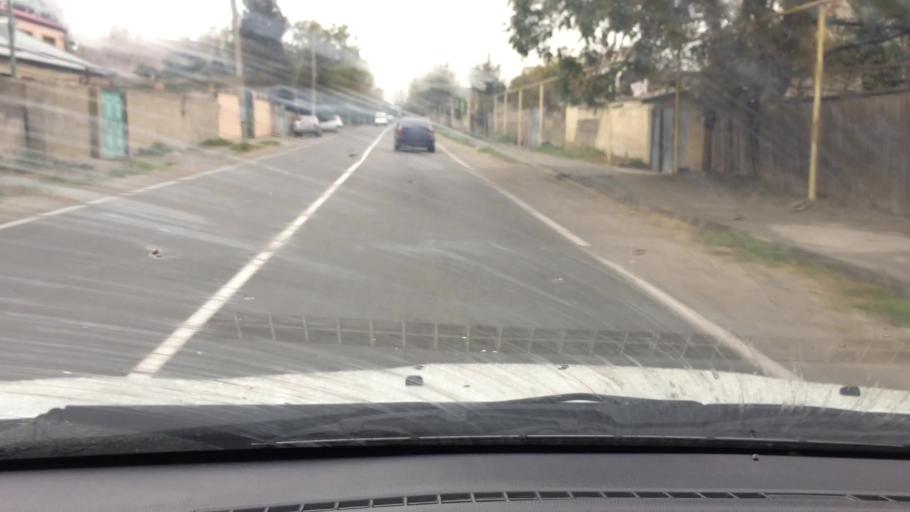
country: GE
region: Kvemo Kartli
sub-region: Marneuli
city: Marneuli
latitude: 41.4804
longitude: 44.7999
